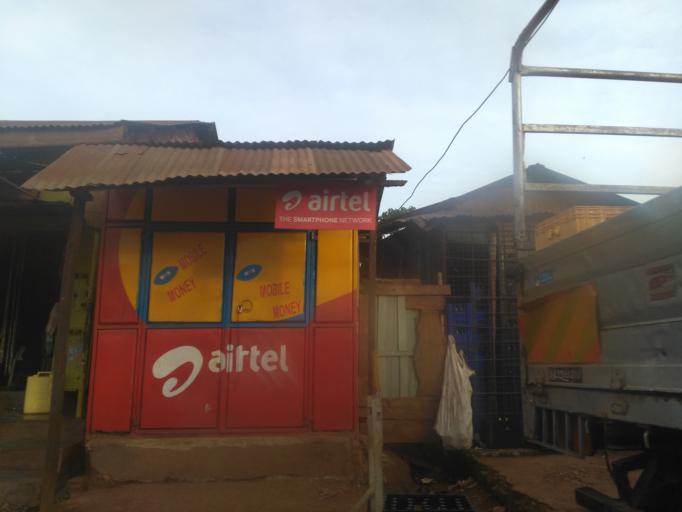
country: UG
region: Central Region
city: Kampala Central Division
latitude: 0.3441
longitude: 32.5765
